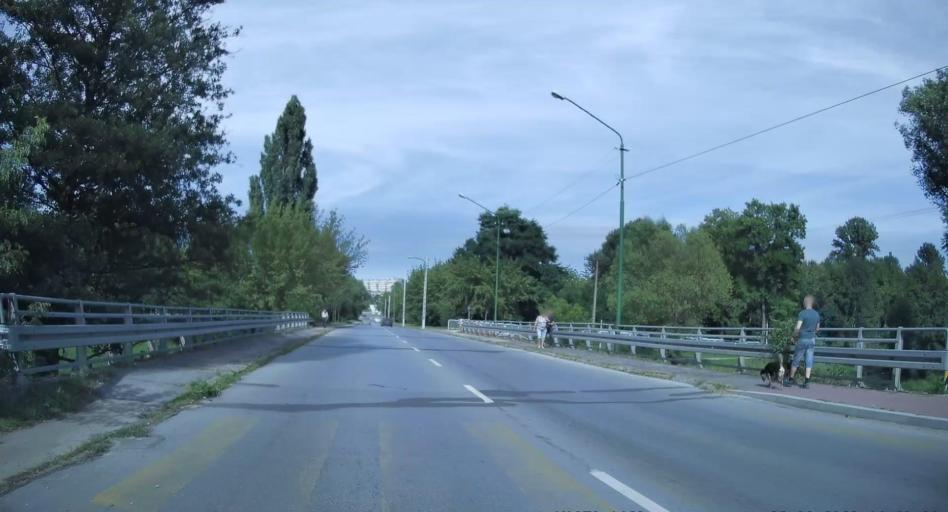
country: PL
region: Lodz Voivodeship
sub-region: Powiat tomaszowski
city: Tomaszow Mazowiecki
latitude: 51.5366
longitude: 19.9975
